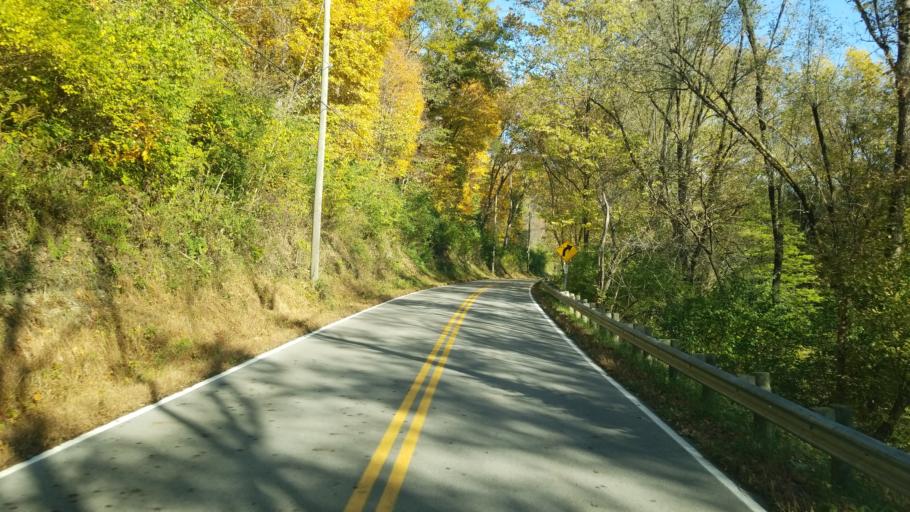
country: US
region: Ohio
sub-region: Warren County
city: Morrow
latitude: 39.3640
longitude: -84.1111
